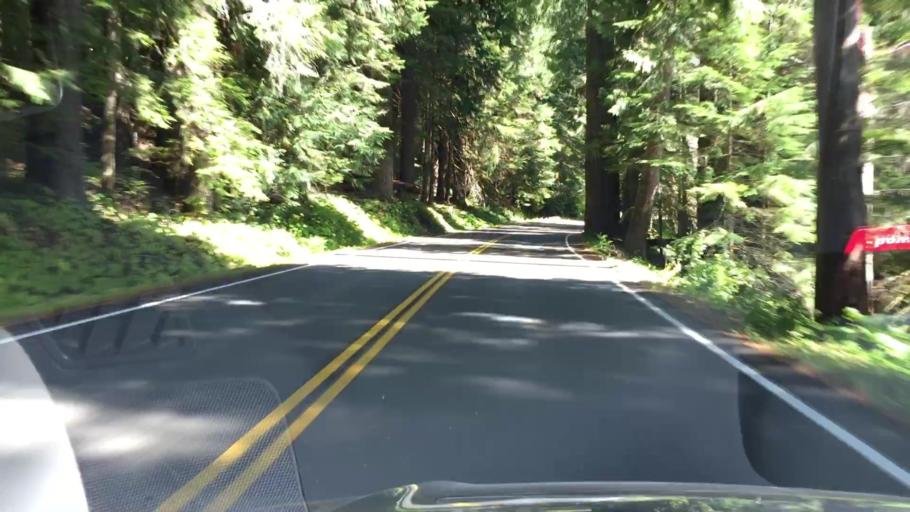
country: US
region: Washington
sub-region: Pierce County
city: Eatonville
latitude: 46.7405
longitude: -121.8833
